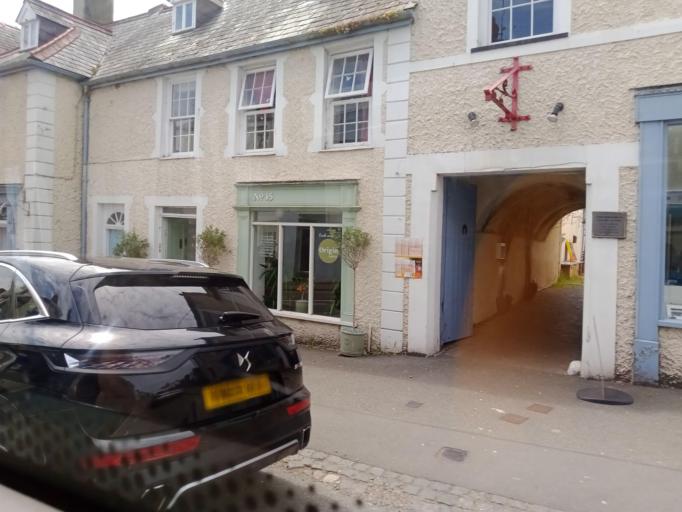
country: GB
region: Wales
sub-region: Anglesey
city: Beaumaris
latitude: 53.2638
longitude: -4.0936
